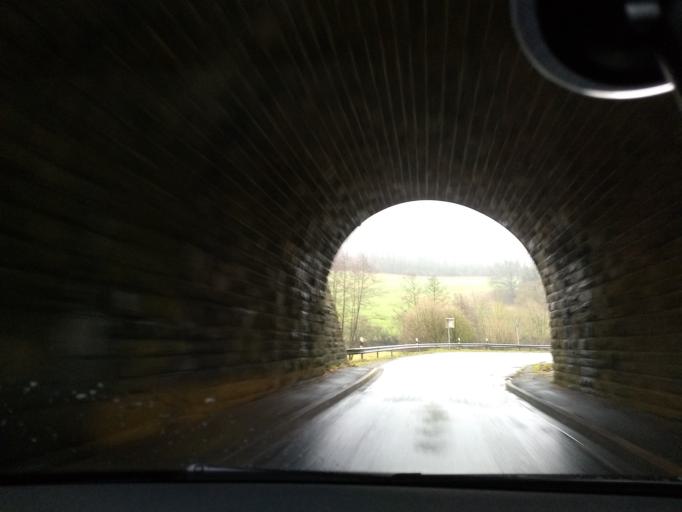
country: DE
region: North Rhine-Westphalia
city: Eslohe
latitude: 51.2565
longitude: 8.1491
